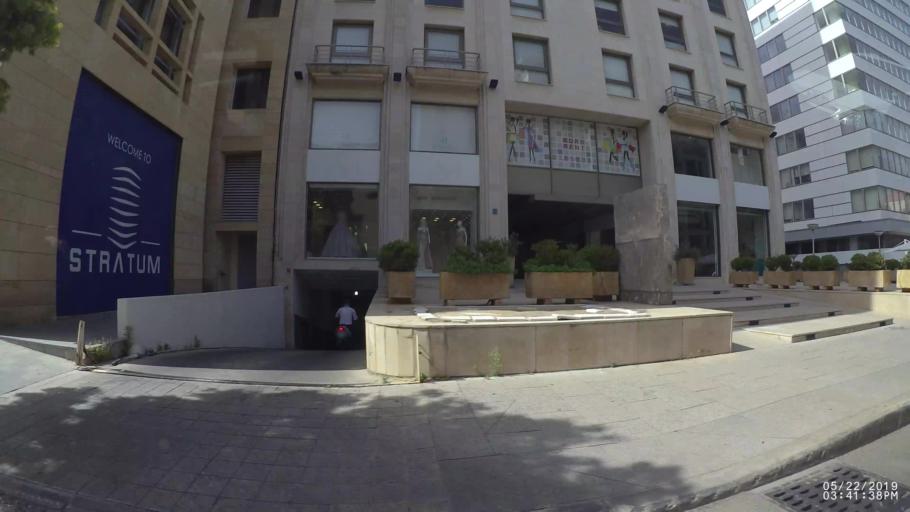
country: LB
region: Beyrouth
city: Beirut
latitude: 33.8988
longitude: 35.4987
